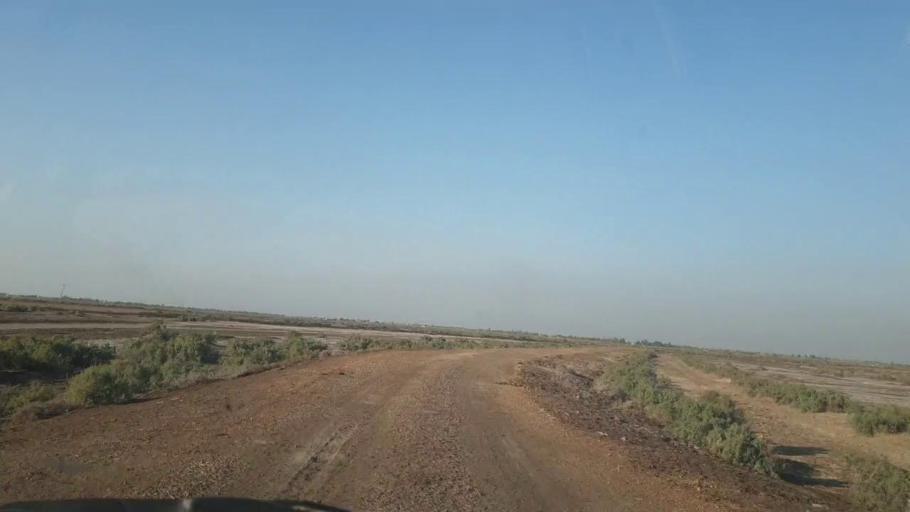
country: PK
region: Sindh
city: Mirpur Khas
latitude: 25.4423
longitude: 69.1017
